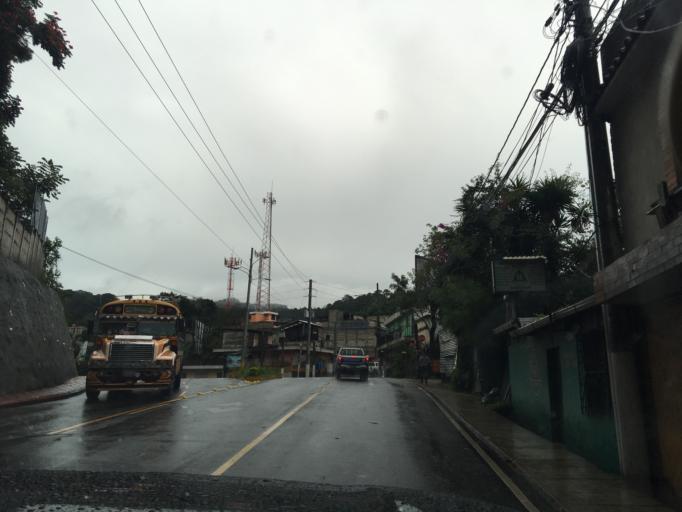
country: GT
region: Guatemala
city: Santa Catarina Pinula
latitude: 14.5654
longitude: -90.4896
